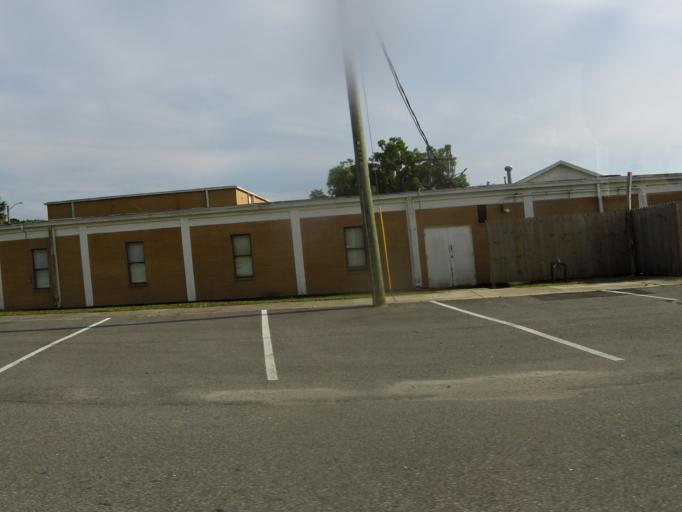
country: US
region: Florida
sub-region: Duval County
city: Jacksonville
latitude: 30.3348
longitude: -81.5957
